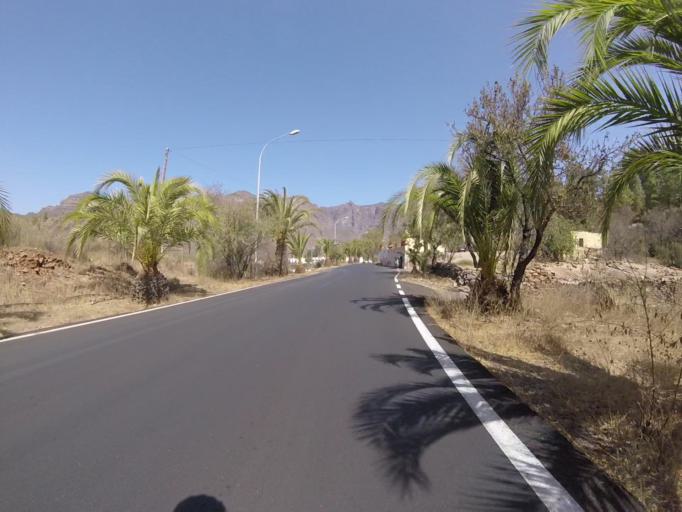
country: ES
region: Canary Islands
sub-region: Provincia de Las Palmas
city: San Bartolome
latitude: 27.9188
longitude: -15.5753
